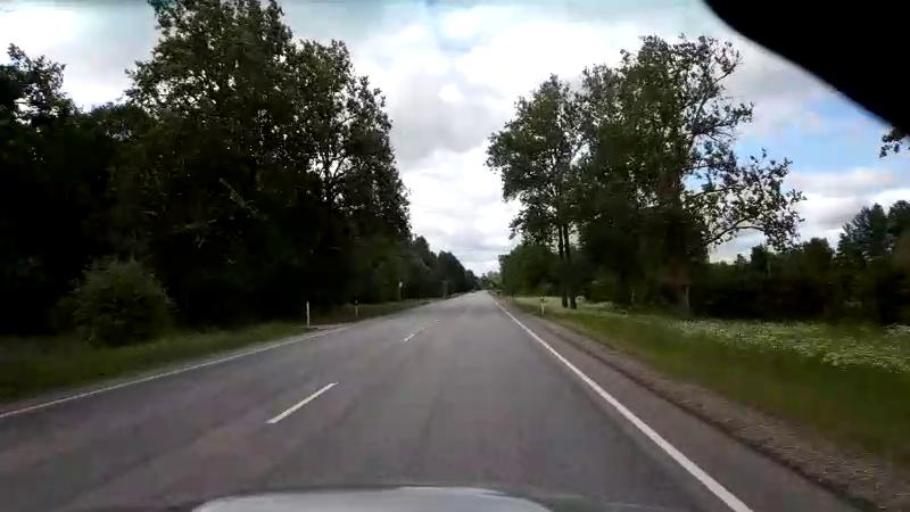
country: EE
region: Harju
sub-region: Nissi vald
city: Riisipere
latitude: 59.1046
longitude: 24.4722
